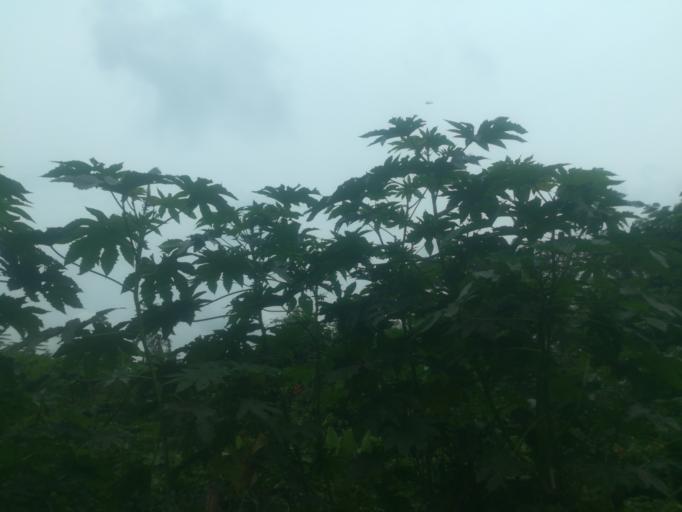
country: NG
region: Ogun
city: Itori
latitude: 7.1005
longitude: 3.1686
